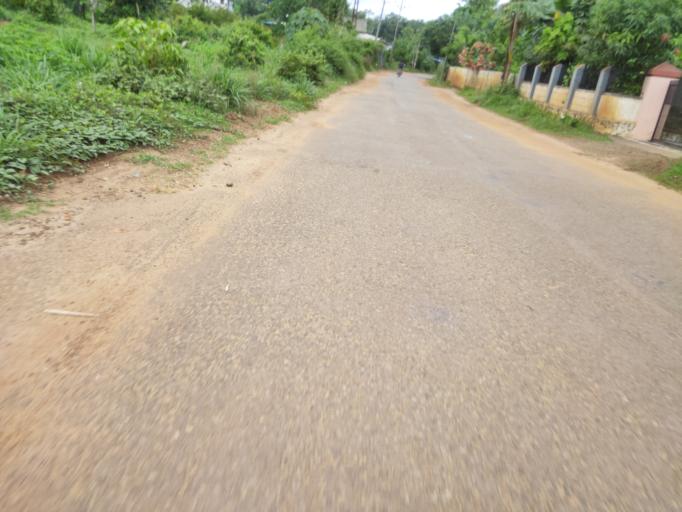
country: IN
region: Kerala
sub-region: Malappuram
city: Manjeri
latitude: 11.2372
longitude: 76.2858
